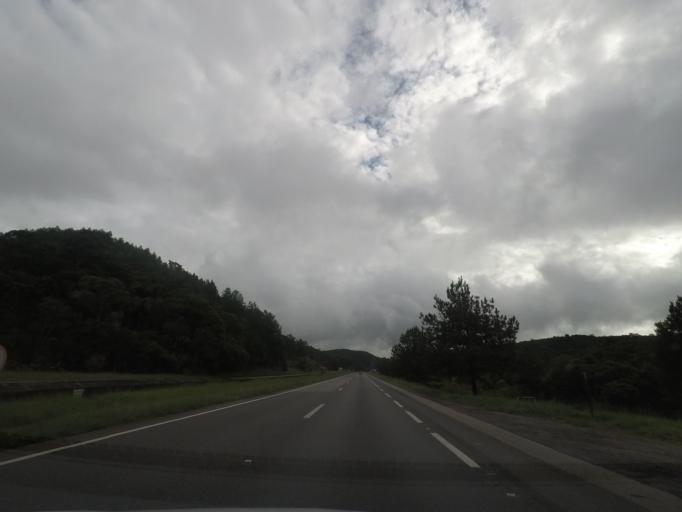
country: BR
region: Parana
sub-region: Campina Grande Do Sul
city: Campina Grande do Sul
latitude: -25.1316
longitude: -48.8572
